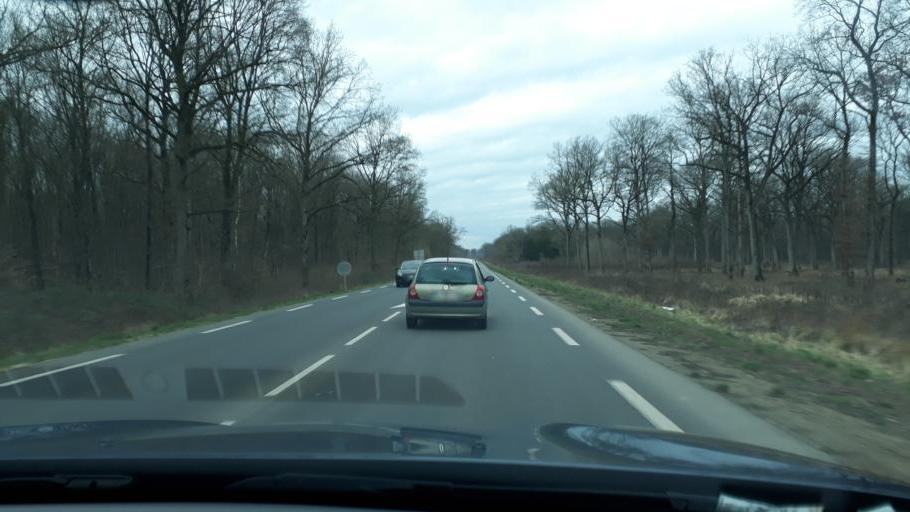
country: FR
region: Centre
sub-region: Departement du Loiret
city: Chanteau
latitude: 48.0081
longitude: 1.9536
